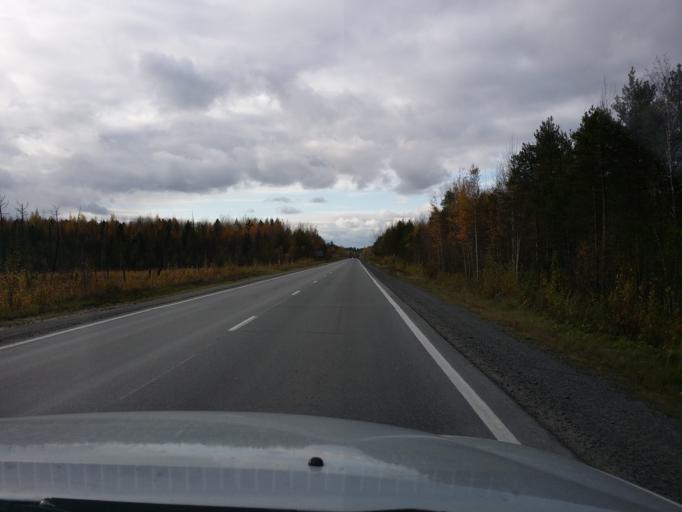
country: RU
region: Khanty-Mansiyskiy Avtonomnyy Okrug
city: Langepas
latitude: 61.2035
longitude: 75.3948
